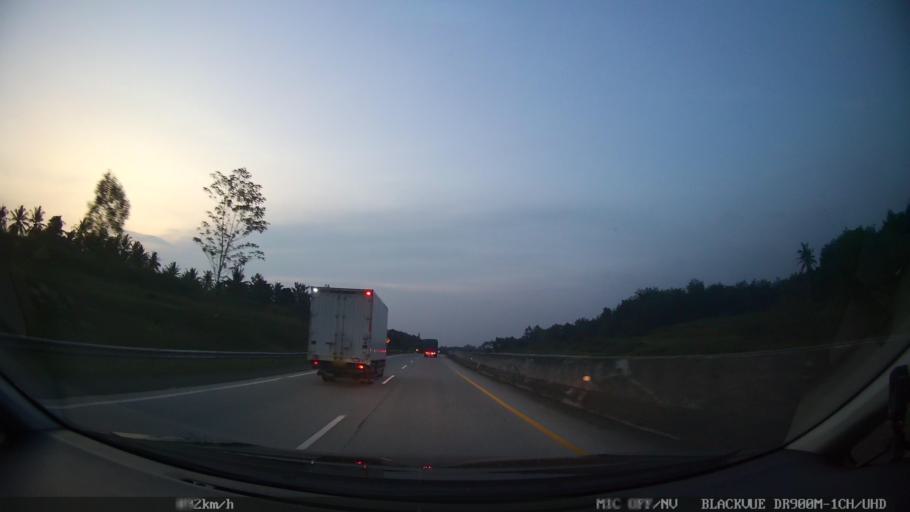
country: ID
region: Lampung
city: Sidorejo
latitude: -5.5595
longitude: 105.5291
